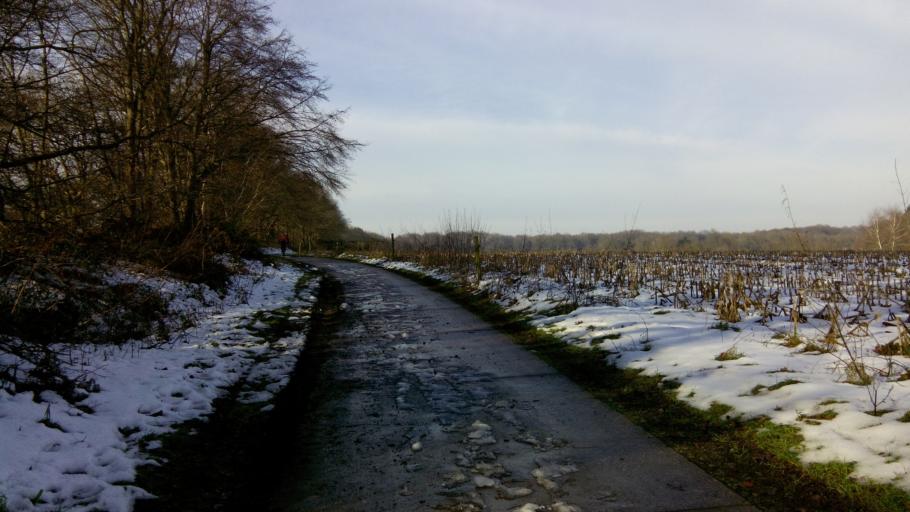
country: NL
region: Gelderland
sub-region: Gemeente Groesbeek
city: Bredeweg
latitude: 51.7401
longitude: 5.9151
